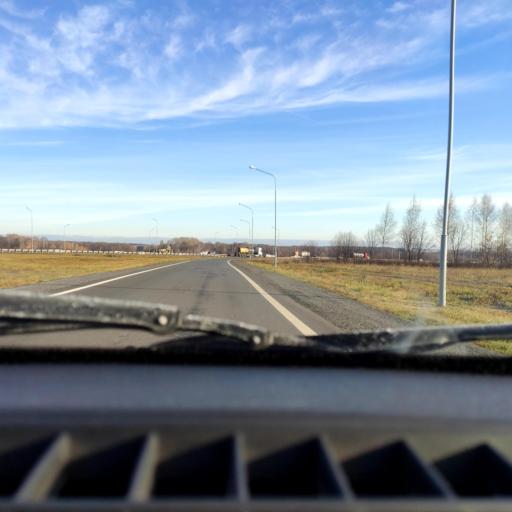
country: RU
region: Bashkortostan
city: Avdon
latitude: 54.6635
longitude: 55.7366
